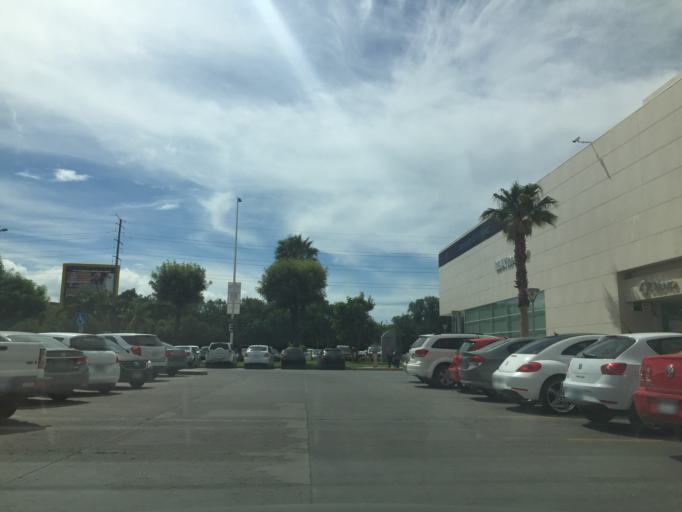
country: MX
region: Guanajuato
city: Leon
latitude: 21.1572
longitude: -101.6939
